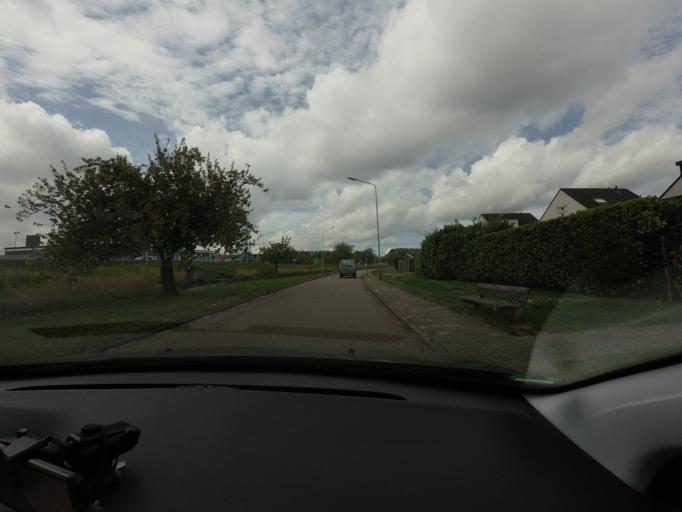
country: NL
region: North Holland
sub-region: Gemeente Landsmeer
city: Landsmeer
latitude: 52.4328
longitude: 4.8743
